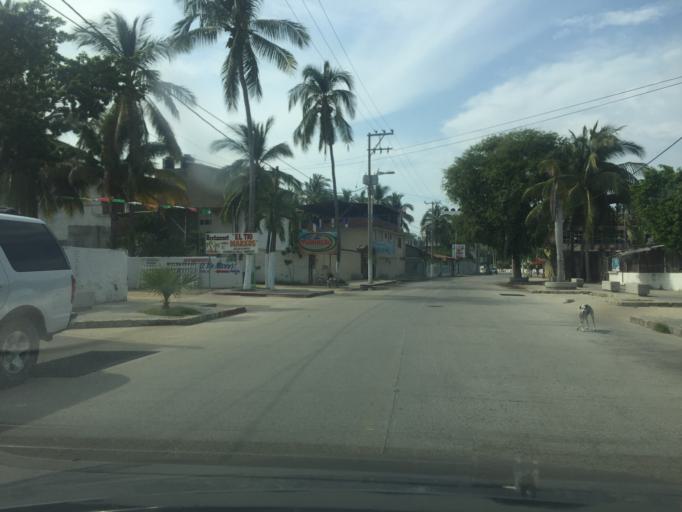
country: MX
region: Guerrero
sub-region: Coyuca de Benitez
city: Colonia Luces en el Mar
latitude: 16.8988
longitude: -99.9657
